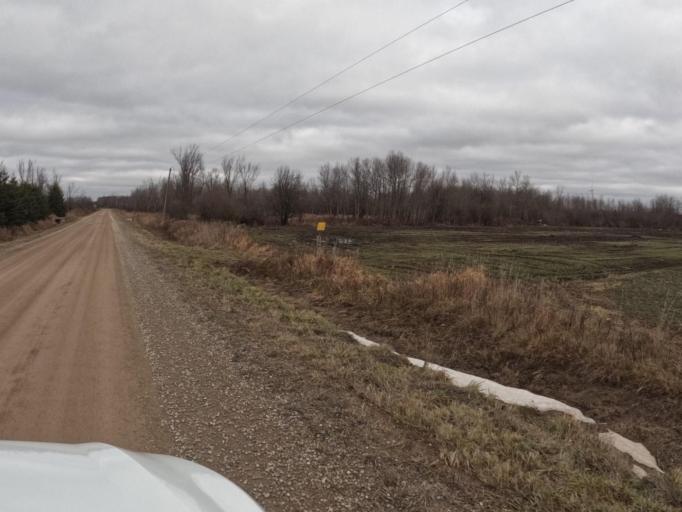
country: CA
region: Ontario
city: Shelburne
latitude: 43.8933
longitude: -80.3837
